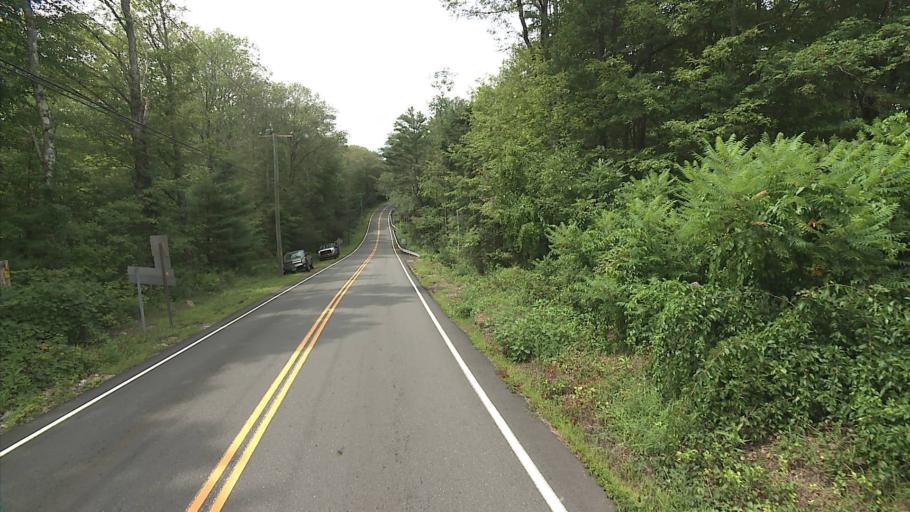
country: US
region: Massachusetts
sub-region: Hampden County
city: Holland
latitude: 41.9846
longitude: -72.1167
